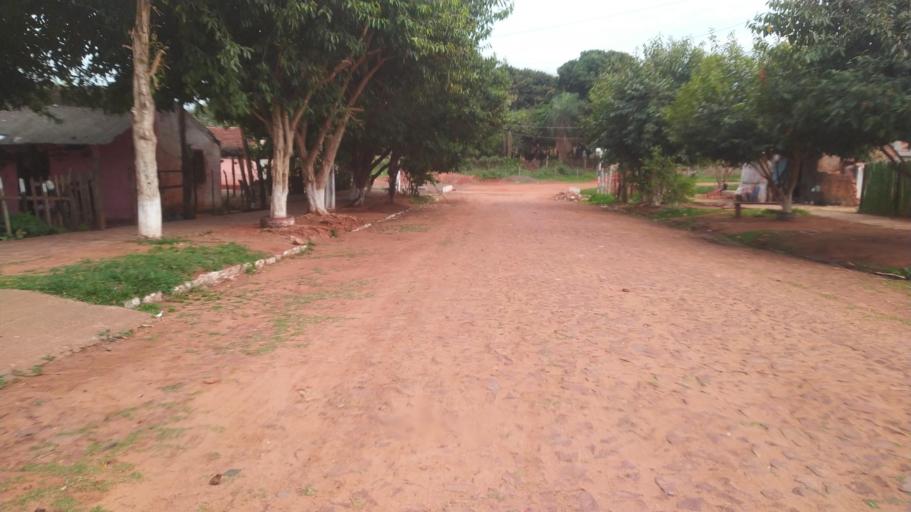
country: PY
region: Misiones
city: San Juan Bautista
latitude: -26.6724
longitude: -57.1534
